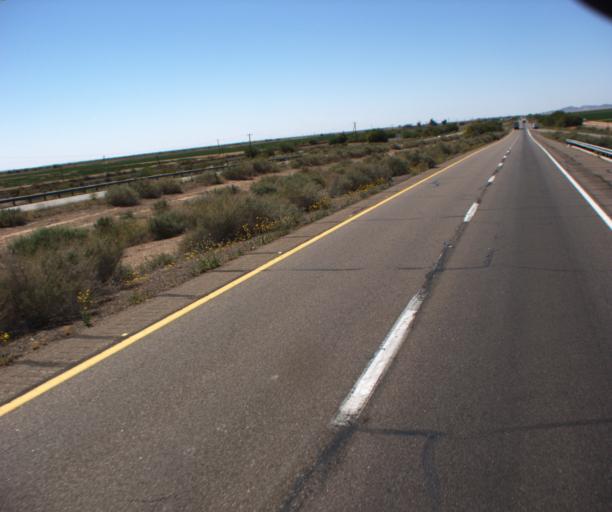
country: US
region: Arizona
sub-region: Maricopa County
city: Gila Bend
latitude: 32.9323
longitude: -112.8057
